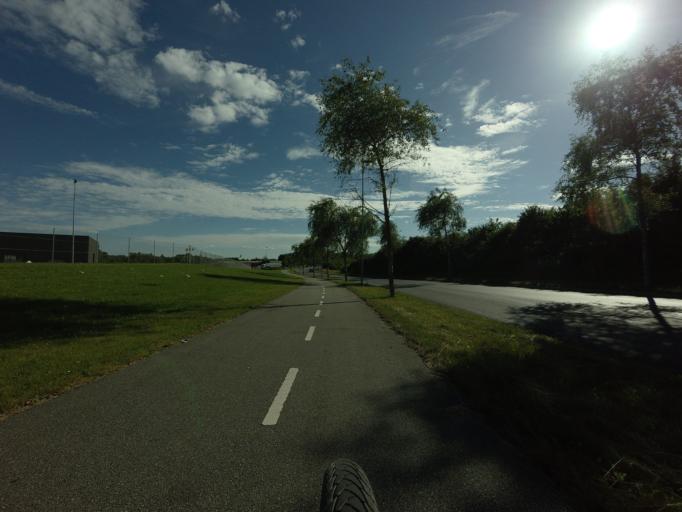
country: DK
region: Central Jutland
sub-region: Skanderborg Kommune
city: Stilling
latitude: 56.0705
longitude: 9.9793
